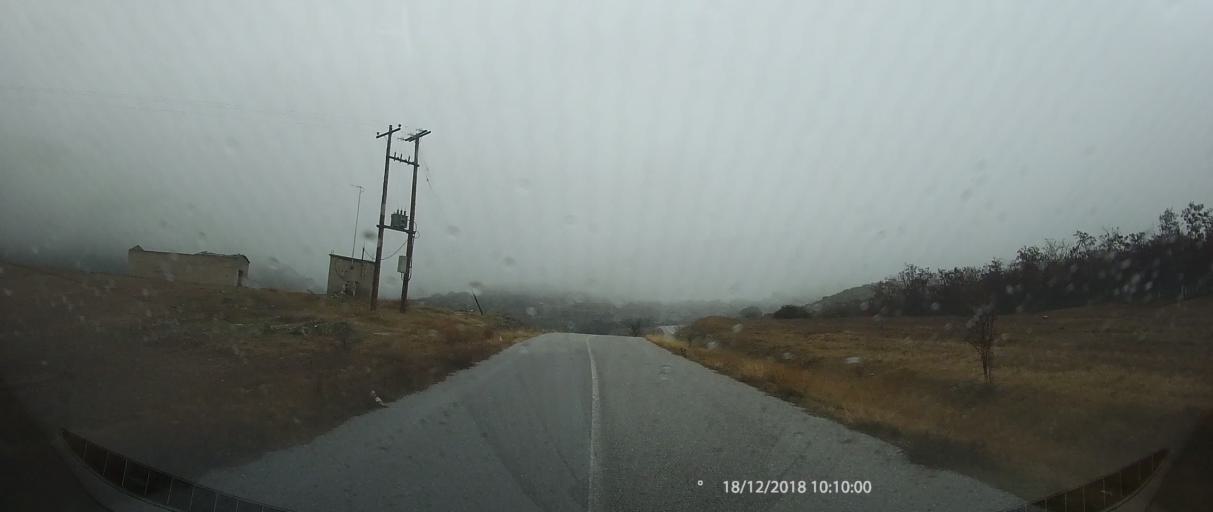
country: GR
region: Thessaly
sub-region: Nomos Larisis
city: Livadi
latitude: 40.0862
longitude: 22.2138
